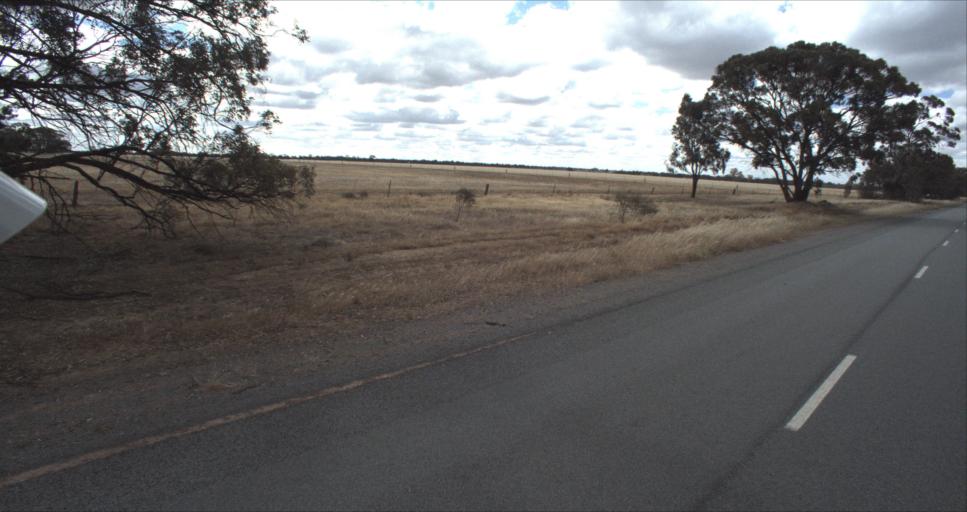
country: AU
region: New South Wales
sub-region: Leeton
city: Leeton
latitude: -34.6806
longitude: 146.3457
